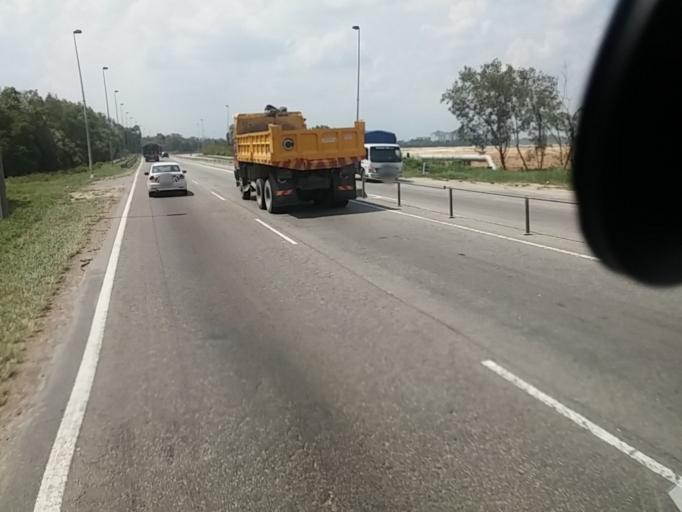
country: MY
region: Selangor
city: Klang
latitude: 2.9851
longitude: 101.3754
